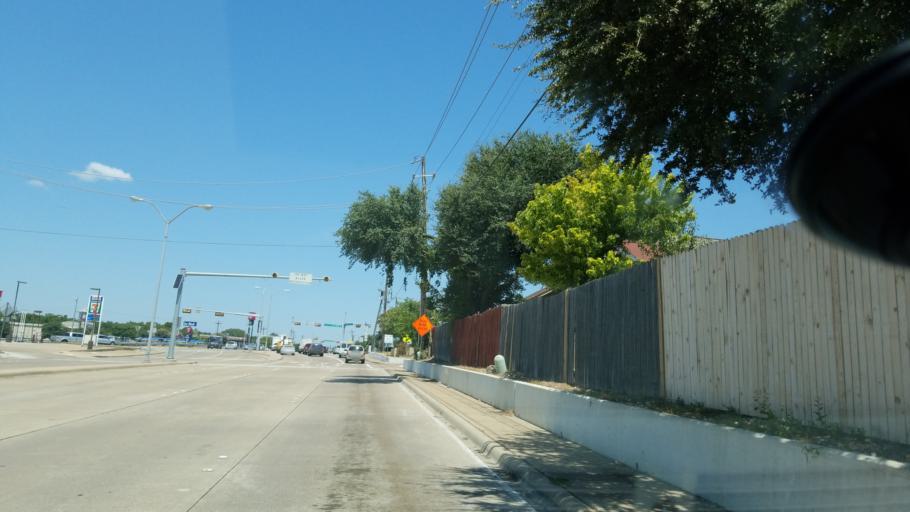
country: US
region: Texas
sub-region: Dallas County
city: Duncanville
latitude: 32.6392
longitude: -96.8912
